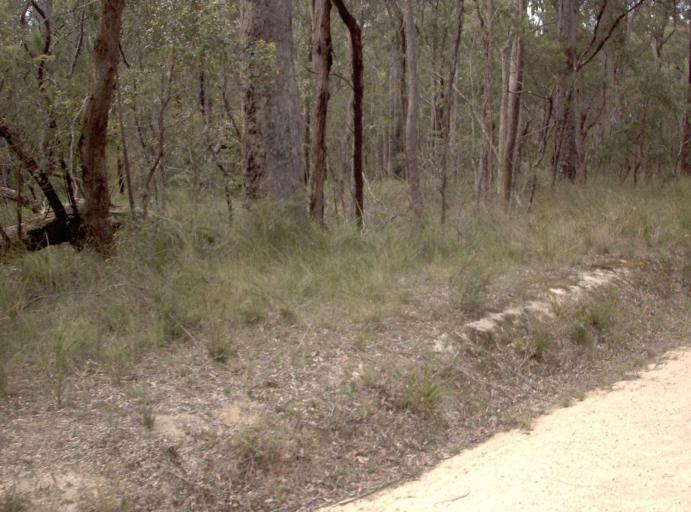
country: AU
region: New South Wales
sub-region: Bega Valley
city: Eden
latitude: -37.4423
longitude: 149.6423
